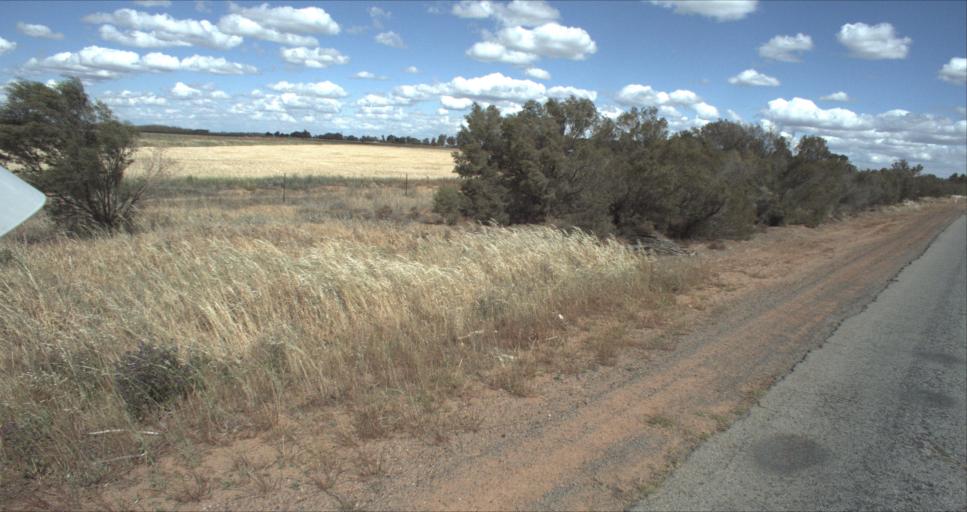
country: AU
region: New South Wales
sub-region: Leeton
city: Leeton
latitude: -34.4779
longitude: 146.2496
